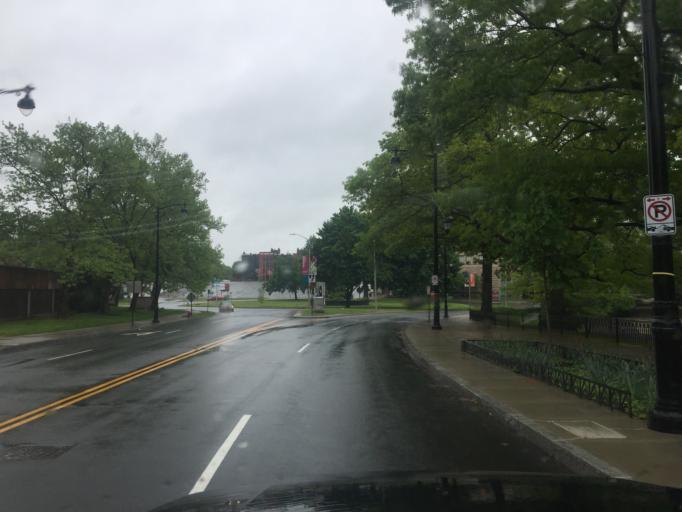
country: US
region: Connecticut
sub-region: Hartford County
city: Hartford
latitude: 41.7641
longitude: -72.6758
